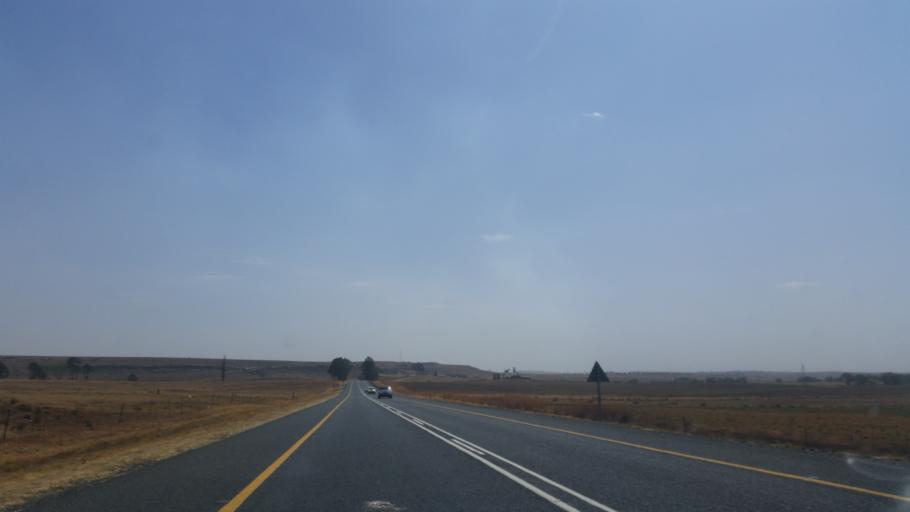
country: ZA
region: Orange Free State
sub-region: Thabo Mofutsanyana District Municipality
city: Bethlehem
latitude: -28.3100
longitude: 28.4916
